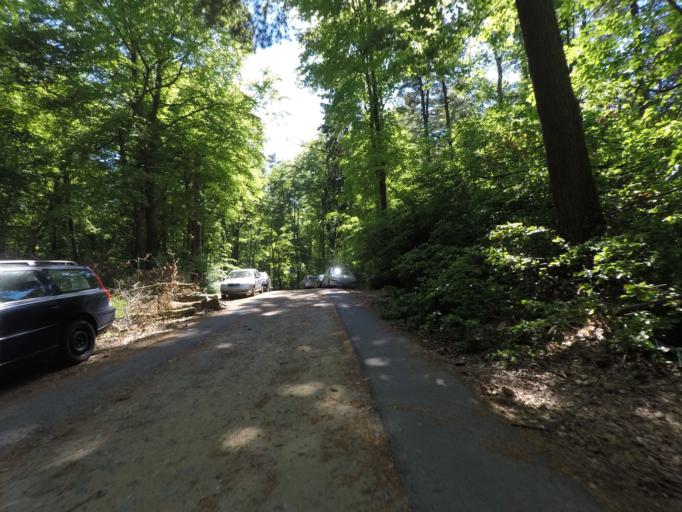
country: DE
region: Brandenburg
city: Eberswalde
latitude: 52.8225
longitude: 13.7792
